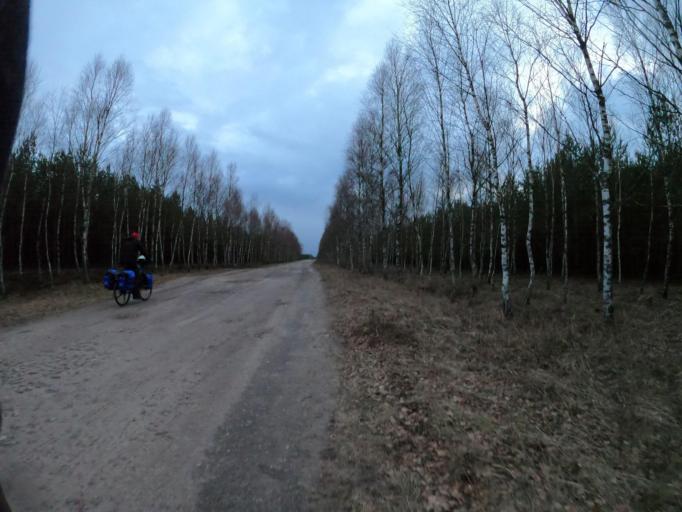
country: PL
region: West Pomeranian Voivodeship
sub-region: Powiat szczecinecki
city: Borne Sulinowo
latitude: 53.5299
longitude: 16.5738
